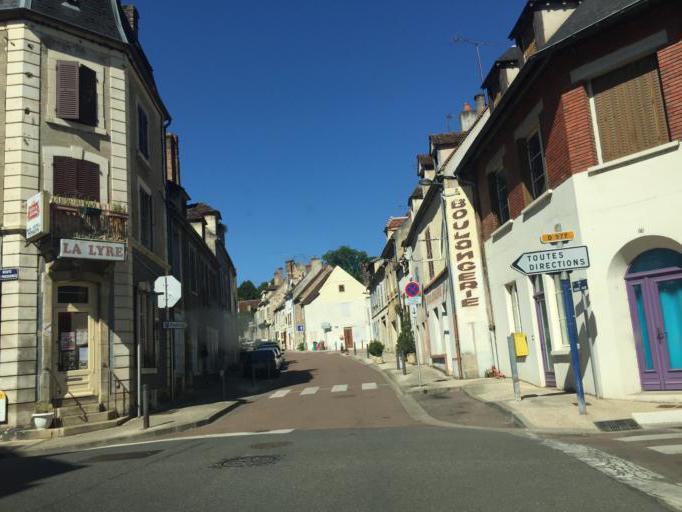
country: FR
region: Bourgogne
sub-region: Departement de la Nievre
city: Clamecy
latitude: 47.4604
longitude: 3.5158
